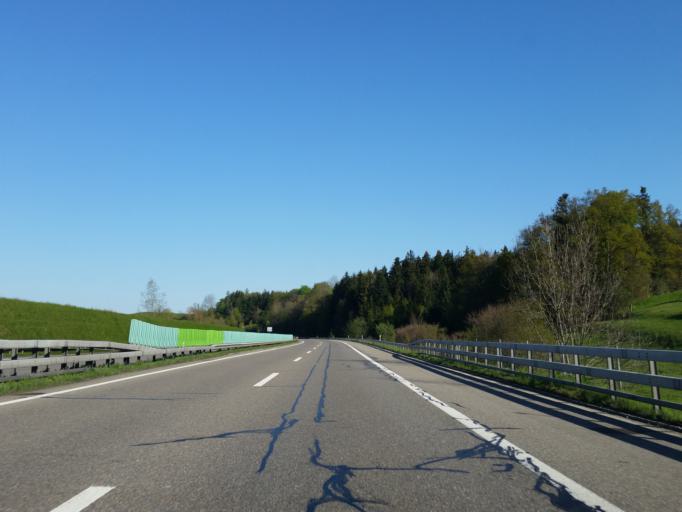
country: CH
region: Saint Gallen
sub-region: Wahlkreis St. Gallen
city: Andwil
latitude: 47.4163
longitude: 9.2763
